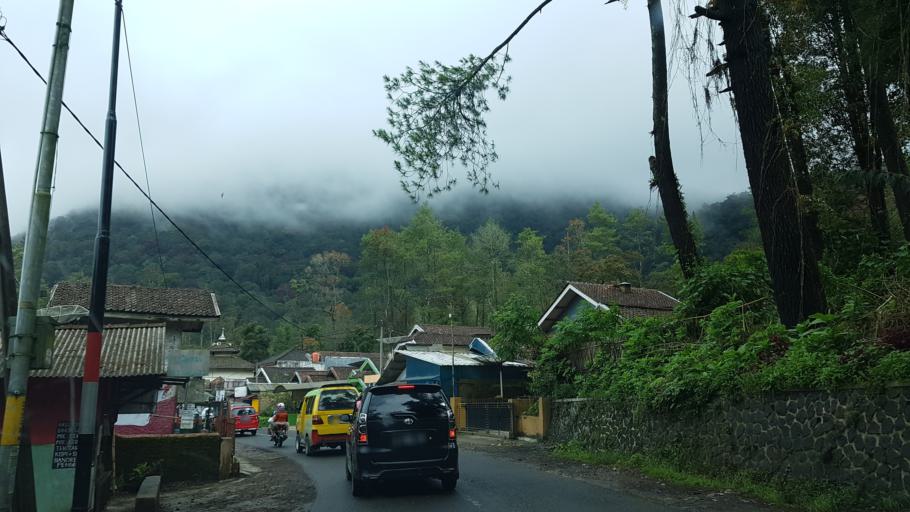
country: ID
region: West Java
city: Banjar
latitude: -7.1457
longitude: 107.3885
